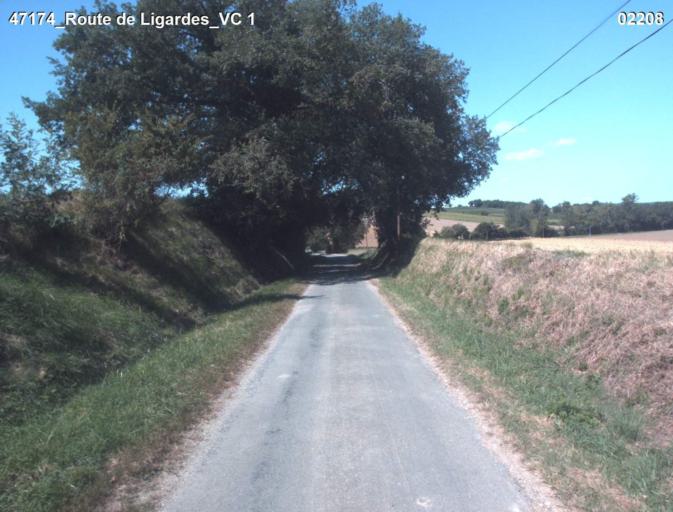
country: FR
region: Midi-Pyrenees
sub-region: Departement du Gers
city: Condom
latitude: 44.0344
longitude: 0.3937
